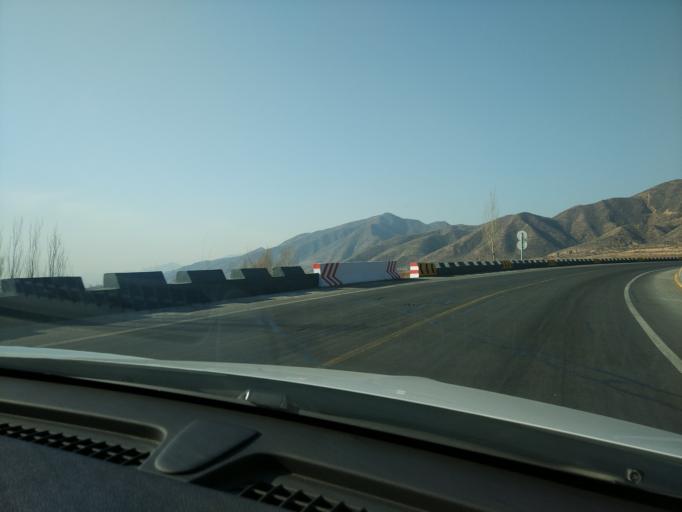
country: CN
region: Hebei
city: Shacheng
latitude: 40.5263
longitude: 115.6185
